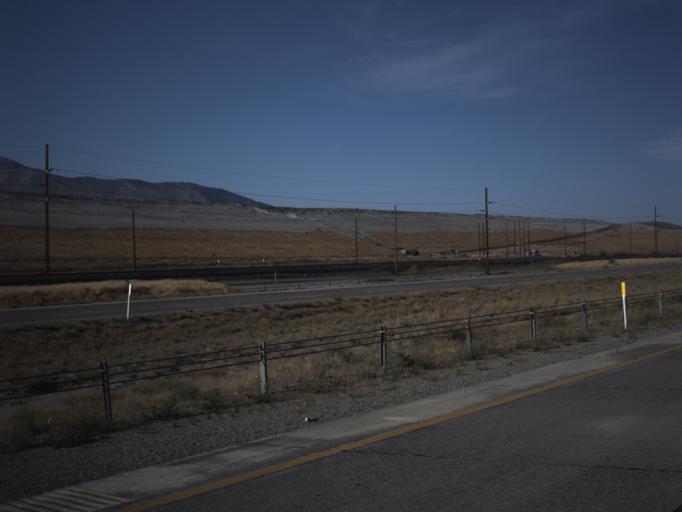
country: US
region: Utah
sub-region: Salt Lake County
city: Magna
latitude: 40.7710
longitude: -112.1325
